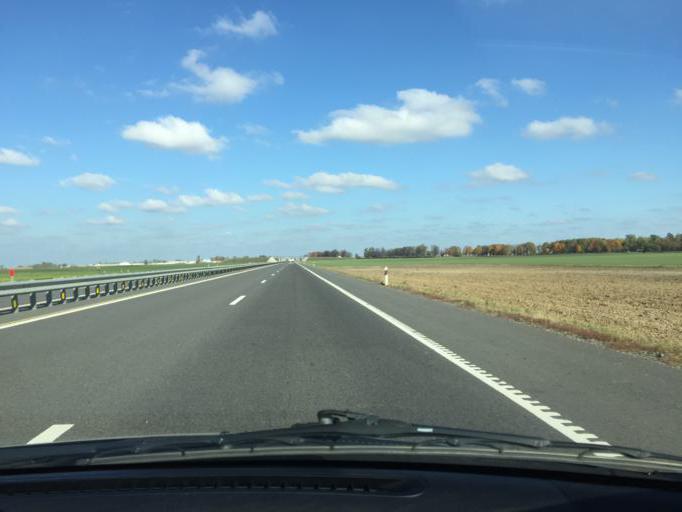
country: BY
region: Minsk
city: Slutsk
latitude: 53.0586
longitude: 27.5438
